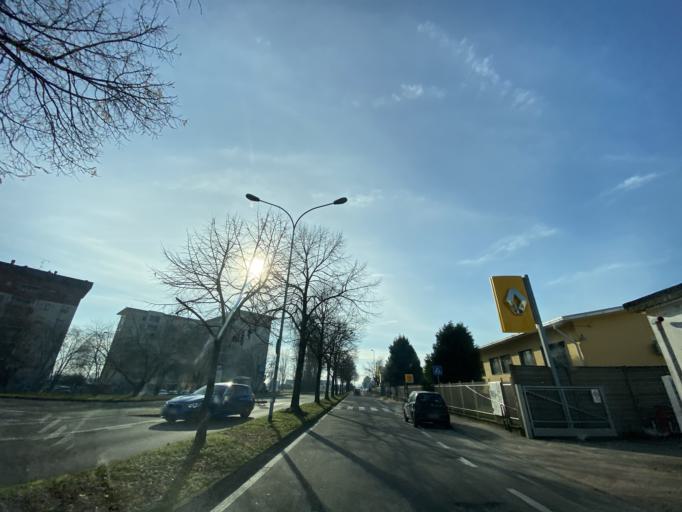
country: IT
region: Lombardy
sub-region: Citta metropolitana di Milano
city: Opera
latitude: 45.3714
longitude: 9.2107
